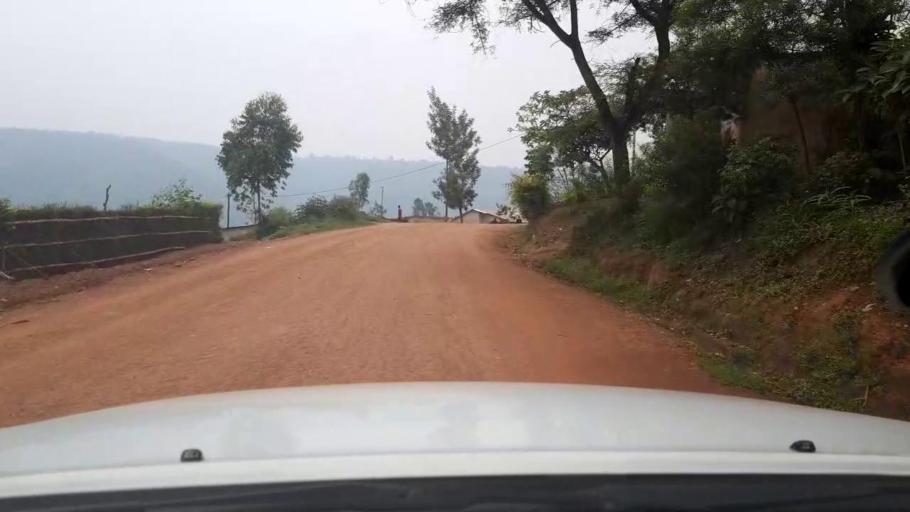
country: RW
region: Kigali
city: Kigali
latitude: -1.9026
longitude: 29.9678
